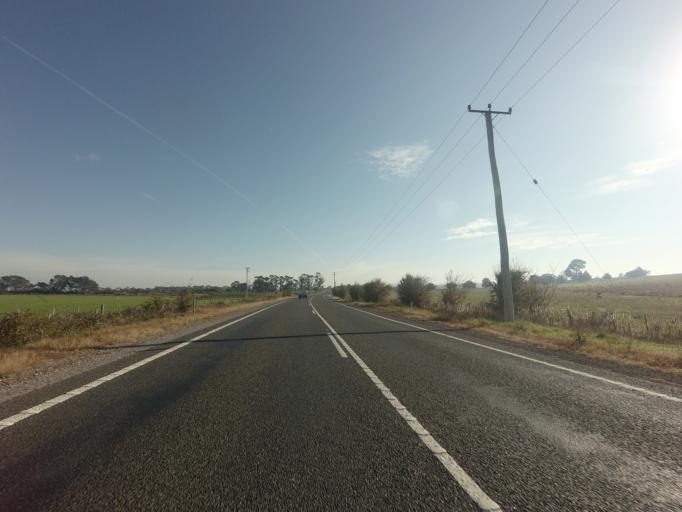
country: AU
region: Tasmania
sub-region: Northern Midlands
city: Longford
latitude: -41.5549
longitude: 147.0631
